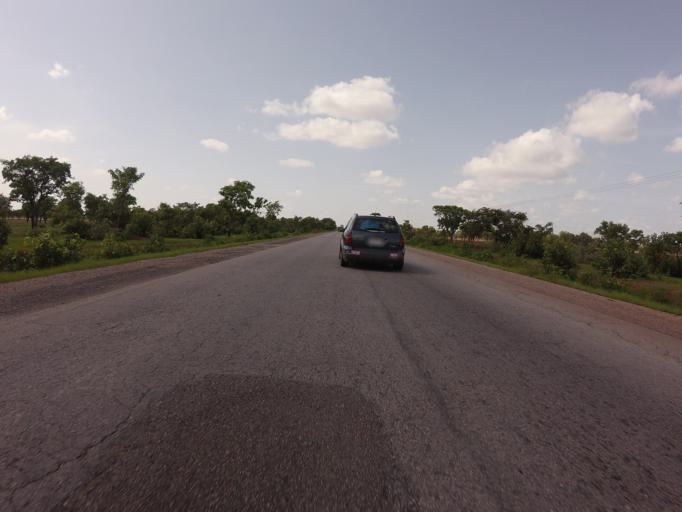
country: GH
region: Northern
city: Savelugu
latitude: 9.9420
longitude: -0.8402
